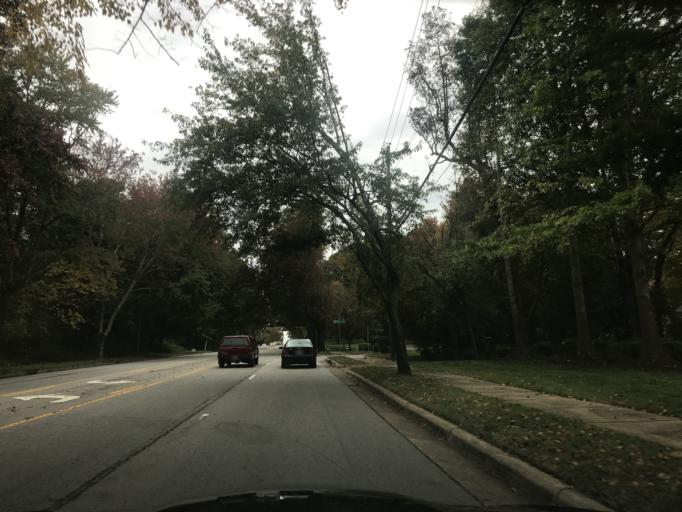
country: US
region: North Carolina
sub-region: Wake County
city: West Raleigh
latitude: 35.8517
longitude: -78.6242
